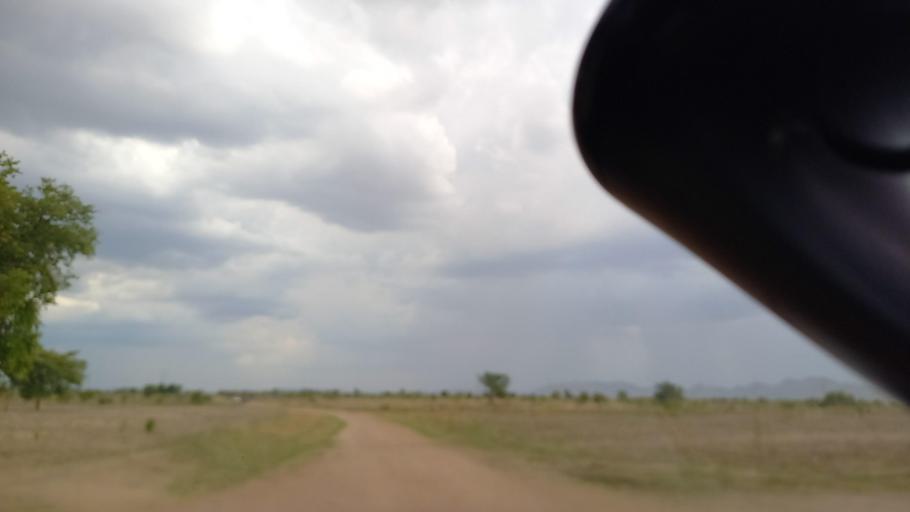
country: ZM
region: Lusaka
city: Kafue
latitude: -15.8443
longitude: 28.0951
